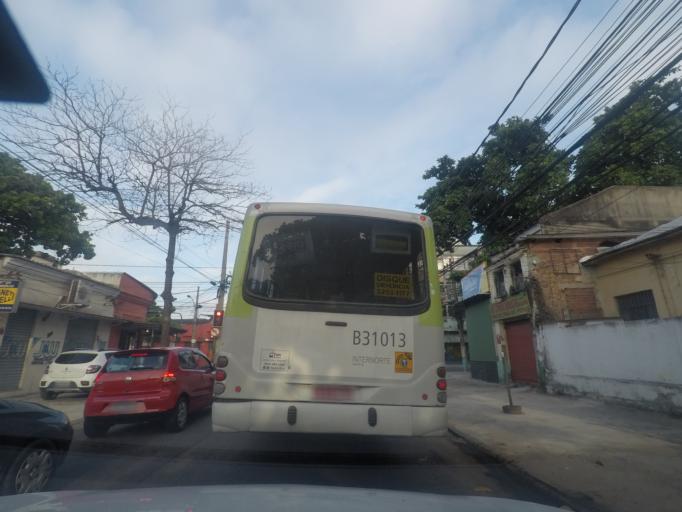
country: BR
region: Rio de Janeiro
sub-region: Duque De Caxias
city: Duque de Caxias
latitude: -22.8366
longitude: -43.2785
